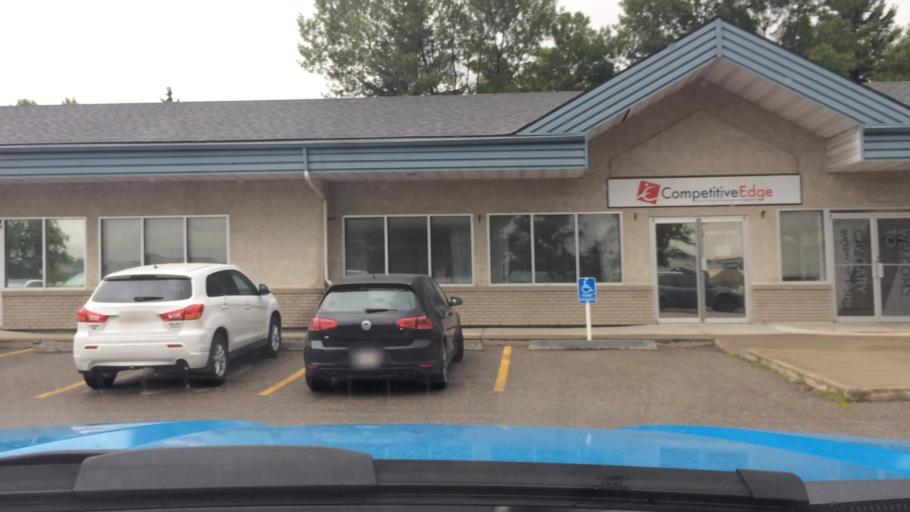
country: CA
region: Alberta
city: Calgary
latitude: 51.0990
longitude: -114.0540
